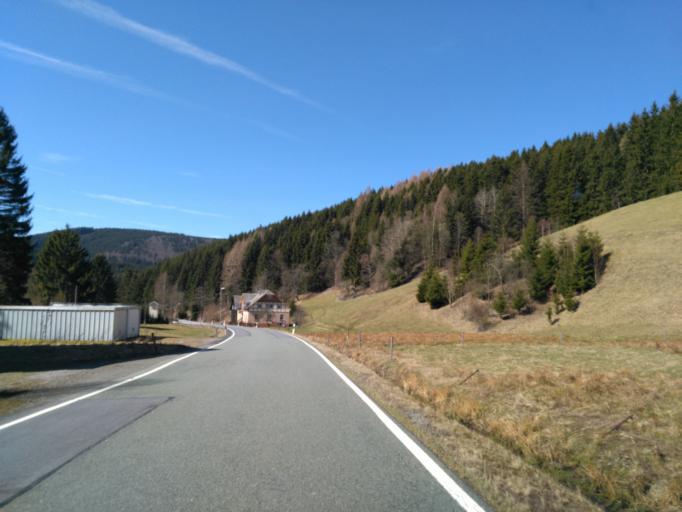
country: DE
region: Saxony
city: Rittersgrun
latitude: 50.4593
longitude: 12.8348
